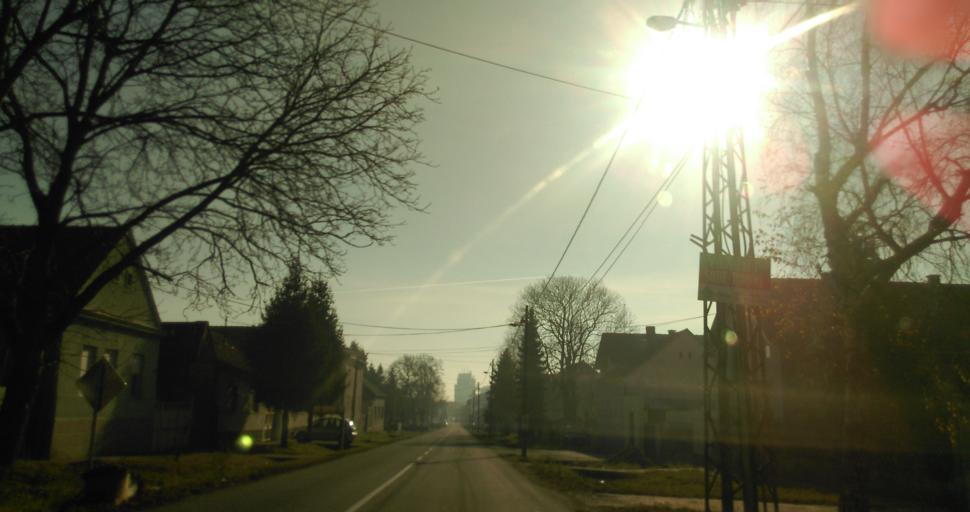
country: RS
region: Autonomna Pokrajina Vojvodina
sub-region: Sremski Okrug
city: Ruma
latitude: 45.0116
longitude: 19.8309
